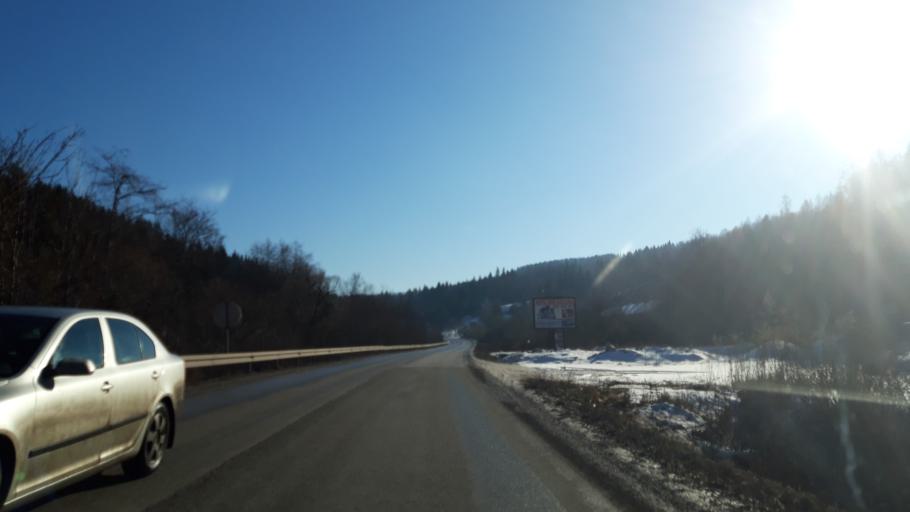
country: BA
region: Republika Srpska
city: Pale
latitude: 43.8449
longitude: 18.5517
